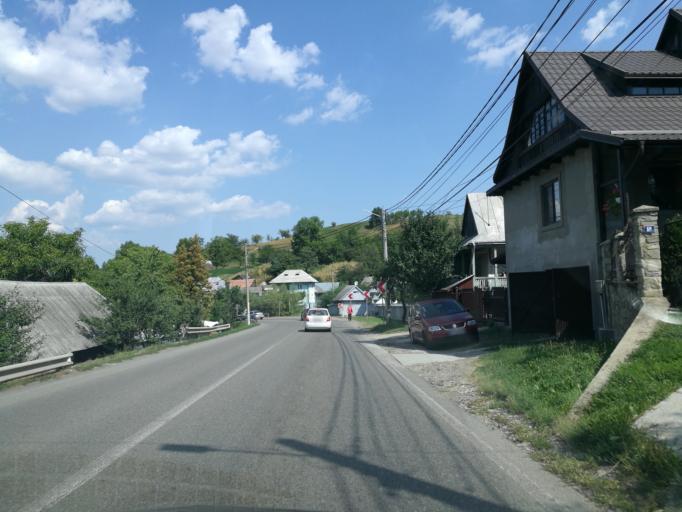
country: RO
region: Neamt
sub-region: Comuna Baltatesti
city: Baltatesti
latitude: 47.1174
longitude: 26.3126
